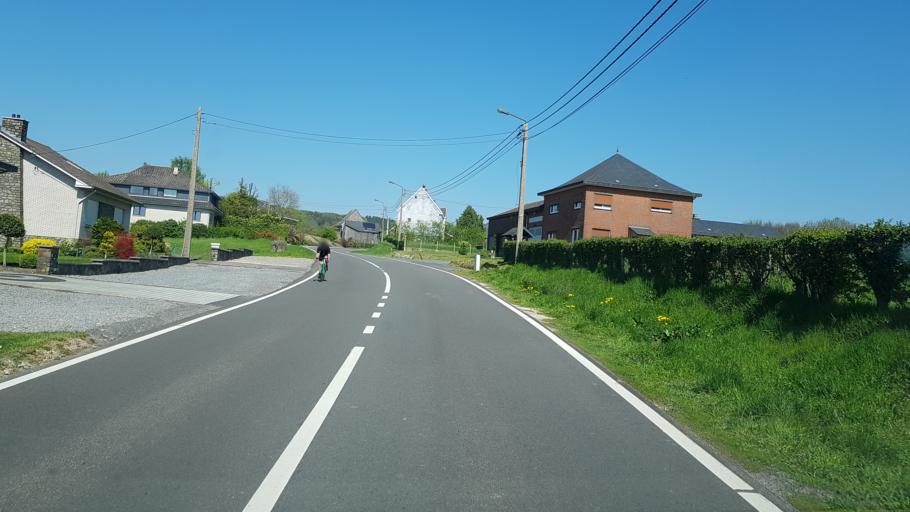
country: BE
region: Wallonia
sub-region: Province de Liege
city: Plombieres
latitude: 50.7431
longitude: 5.9721
